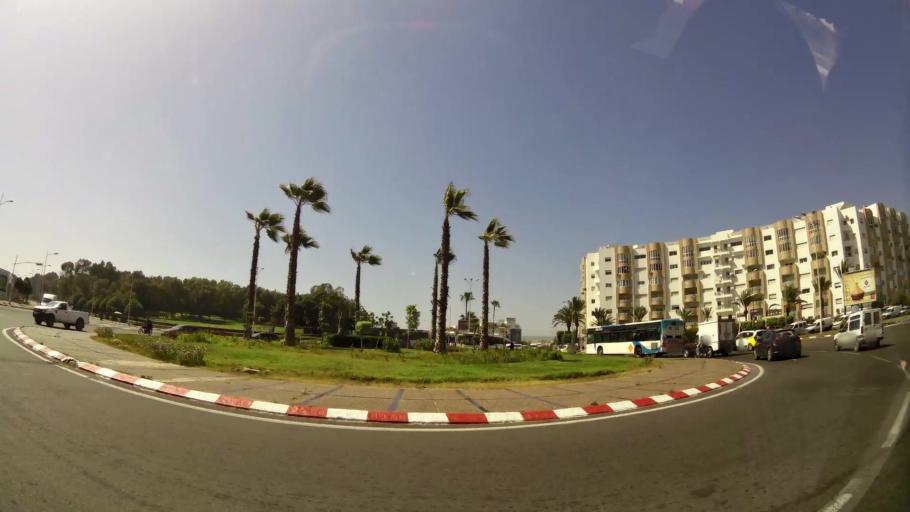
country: MA
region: Souss-Massa-Draa
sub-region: Agadir-Ida-ou-Tnan
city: Agadir
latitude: 30.4074
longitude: -9.5876
